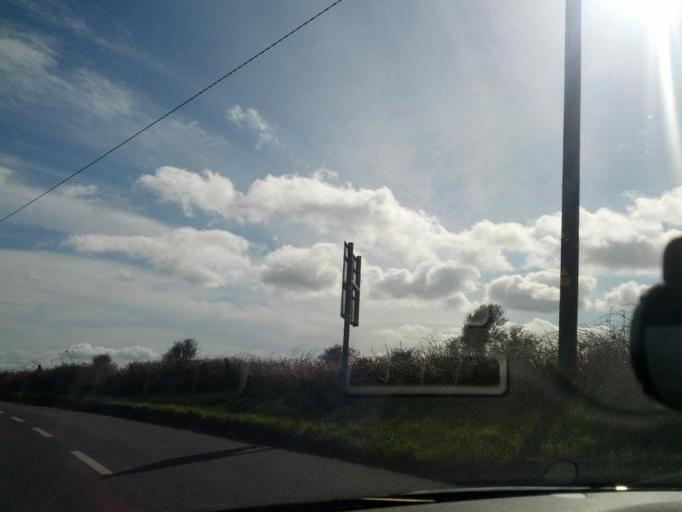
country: IE
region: Leinster
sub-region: Fingal County
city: Baldoyle
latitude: 53.4077
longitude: -6.1356
